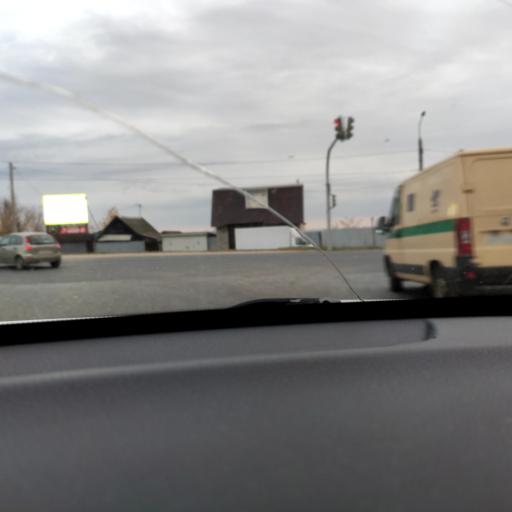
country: RU
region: Tatarstan
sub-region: Zelenodol'skiy Rayon
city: Zelenodolsk
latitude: 55.8455
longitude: 48.5533
